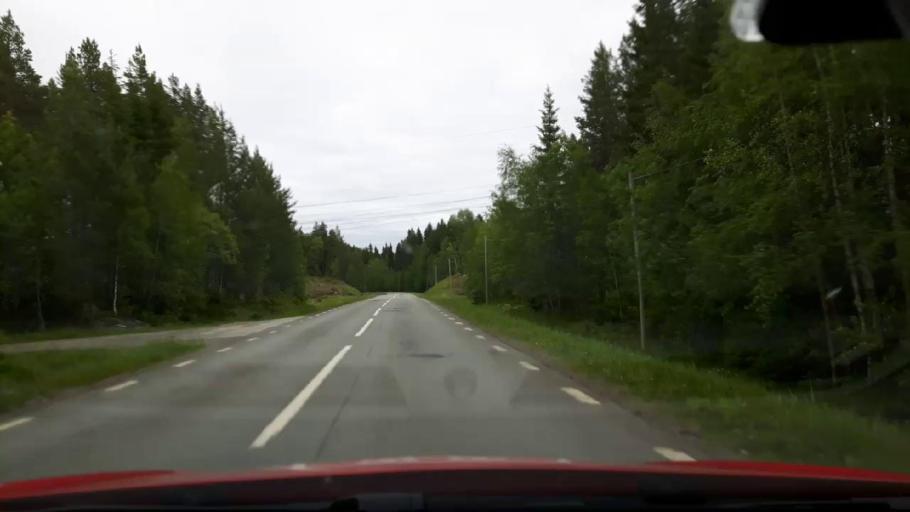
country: SE
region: Jaemtland
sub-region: Stroemsunds Kommun
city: Stroemsund
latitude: 63.3931
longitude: 15.6662
